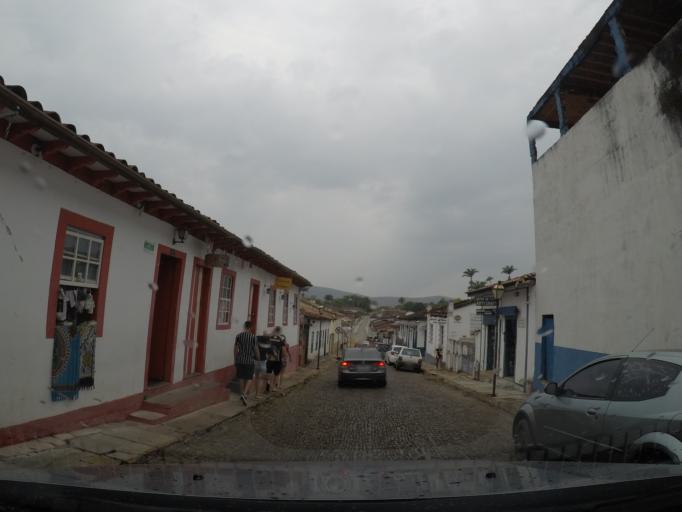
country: BR
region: Goias
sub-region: Pirenopolis
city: Pirenopolis
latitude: -15.8516
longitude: -48.9588
